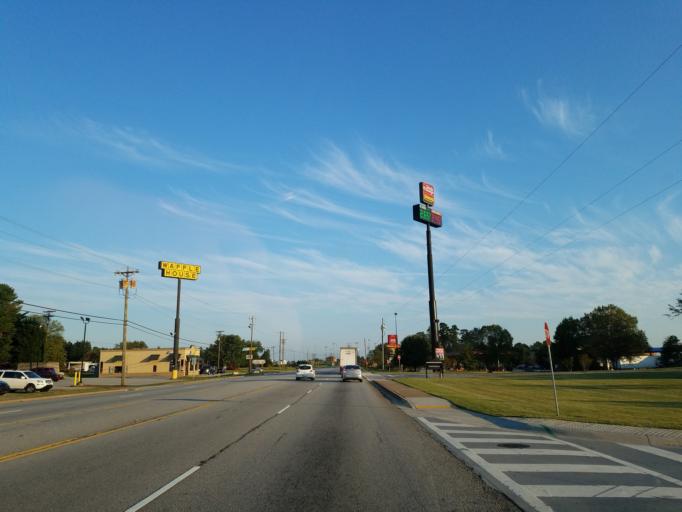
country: US
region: South Carolina
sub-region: Cherokee County
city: Gaffney
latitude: 35.0798
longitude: -81.7039
